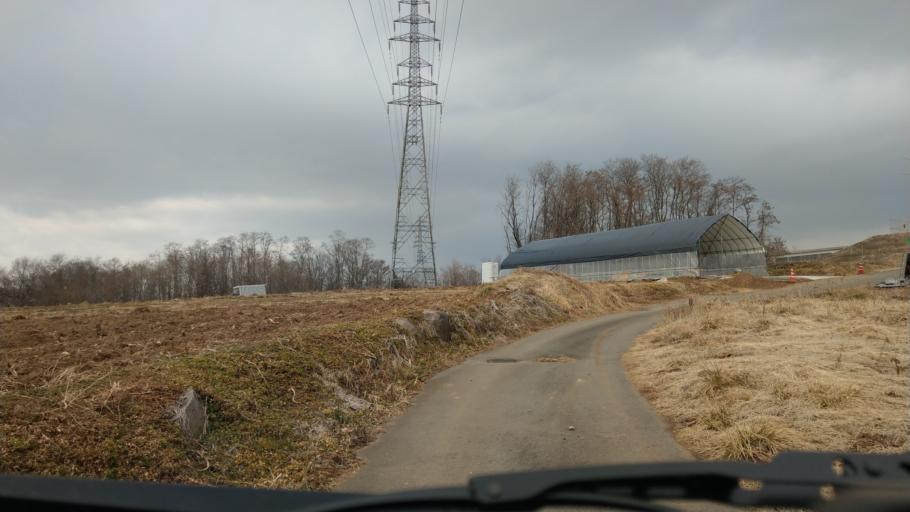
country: JP
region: Nagano
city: Komoro
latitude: 36.3447
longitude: 138.4006
